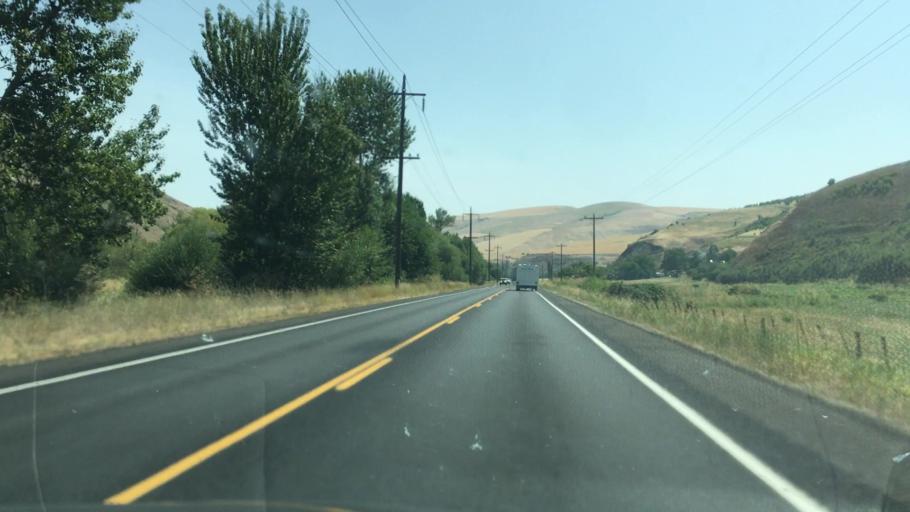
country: US
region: Idaho
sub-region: Nez Perce County
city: Lapwai
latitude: 46.3579
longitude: -116.7850
